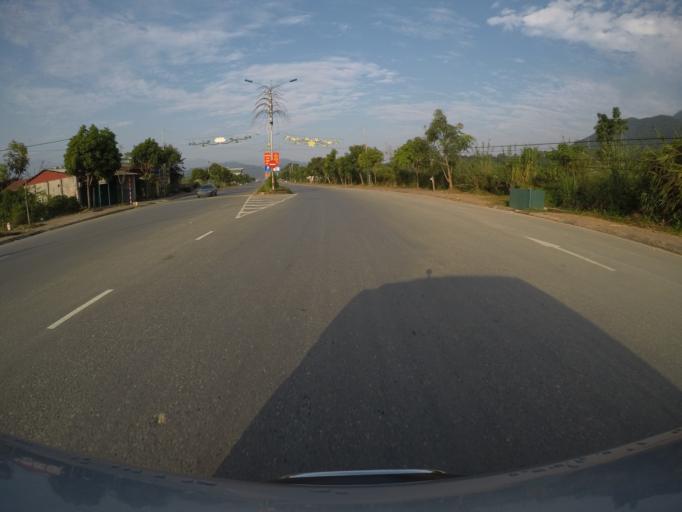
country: VN
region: Lai Chau
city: Tam Duong
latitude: 22.3199
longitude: 103.6364
